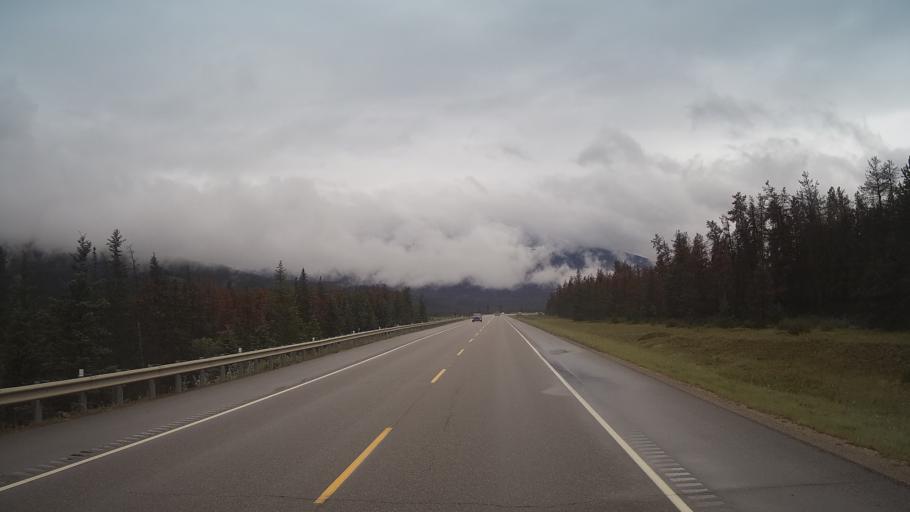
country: CA
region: Alberta
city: Jasper Park Lodge
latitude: 52.9535
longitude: -118.0431
